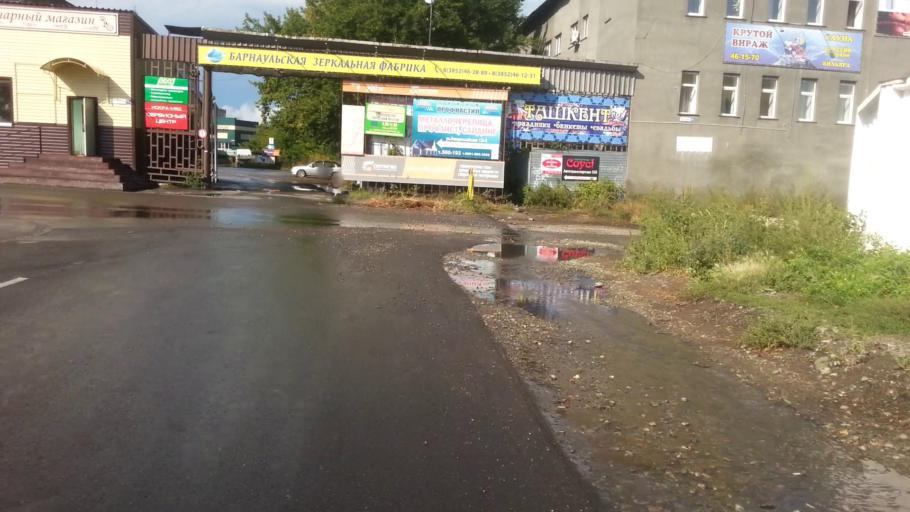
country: RU
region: Altai Krai
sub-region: Gorod Barnaulskiy
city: Barnaul
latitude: 53.3442
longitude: 83.7231
